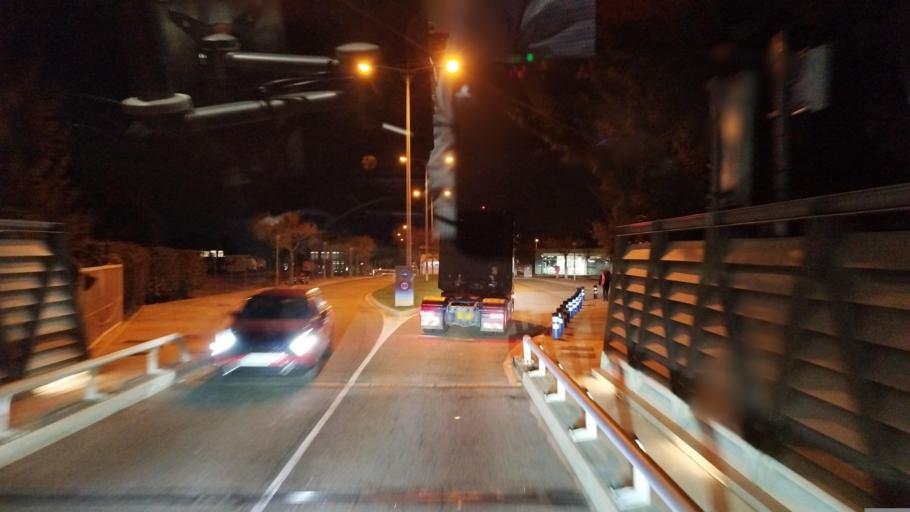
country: ES
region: Catalonia
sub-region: Provincia de Tarragona
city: Santa Oliva
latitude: 41.2679
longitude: 1.5235
